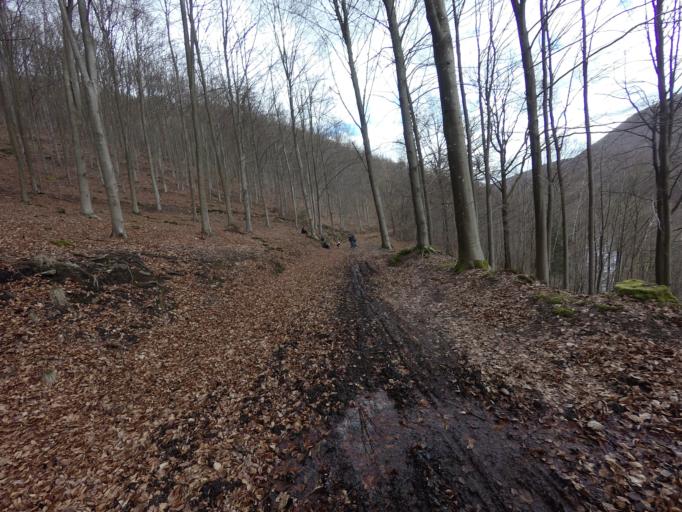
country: BE
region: Wallonia
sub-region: Province de Liege
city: Aywaille
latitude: 50.4278
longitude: 5.7286
